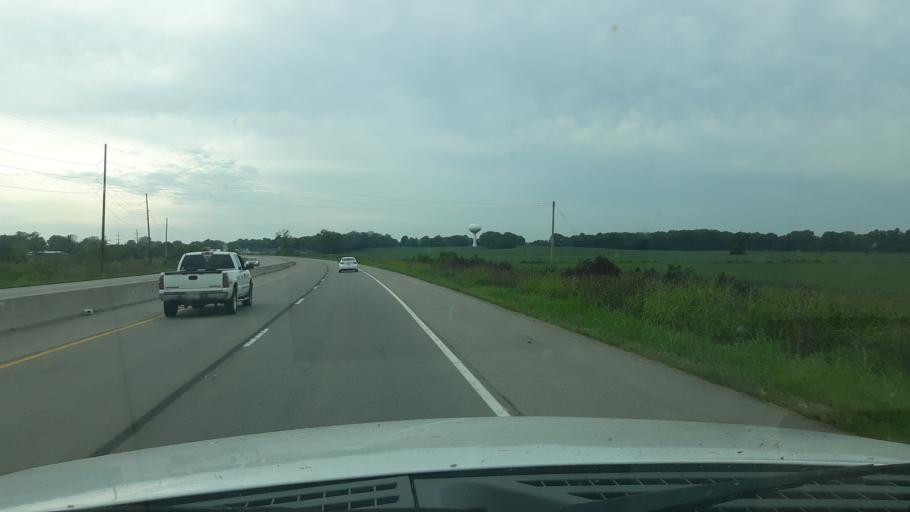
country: US
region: Illinois
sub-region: Saline County
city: Harrisburg
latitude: 37.7433
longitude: -88.5514
